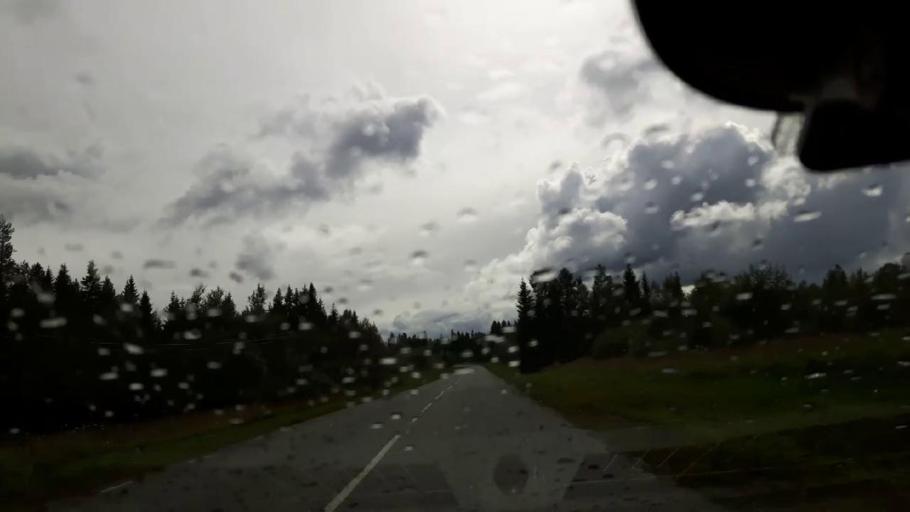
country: SE
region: Jaemtland
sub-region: Krokoms Kommun
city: Valla
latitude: 63.3933
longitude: 13.8203
